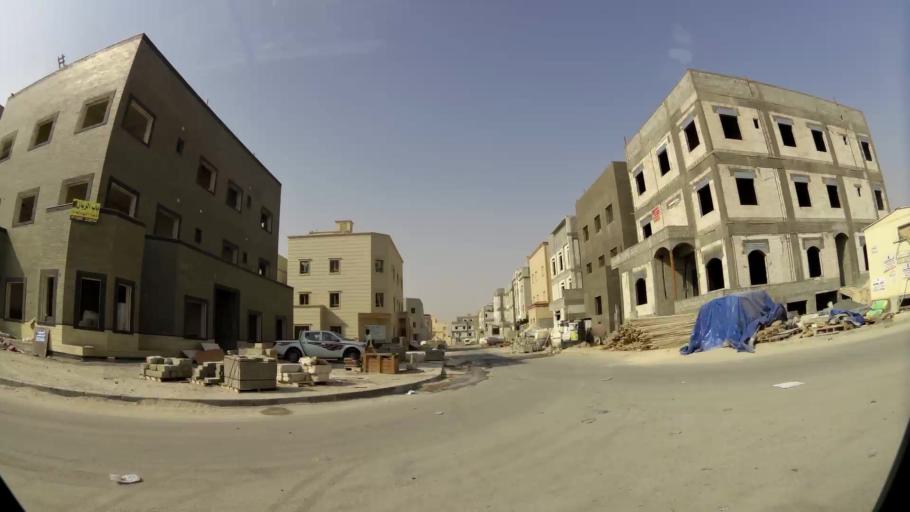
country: KW
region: Muhafazat al Jahra'
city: Al Jahra'
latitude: 29.3489
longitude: 47.7434
